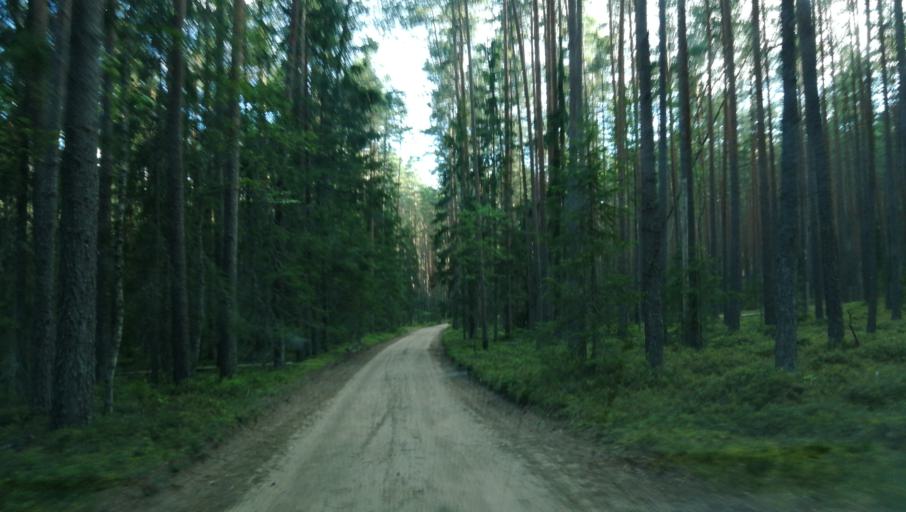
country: LV
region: Cesu Rajons
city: Cesis
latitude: 57.2954
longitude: 25.2064
